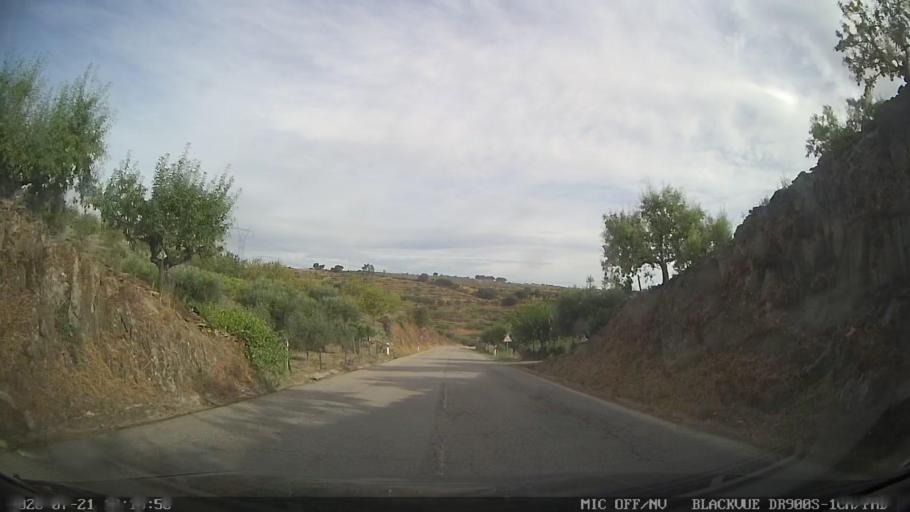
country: PT
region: Guarda
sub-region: Vila Nova de Foz Coa
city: Custoias
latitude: 41.0945
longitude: -7.3726
